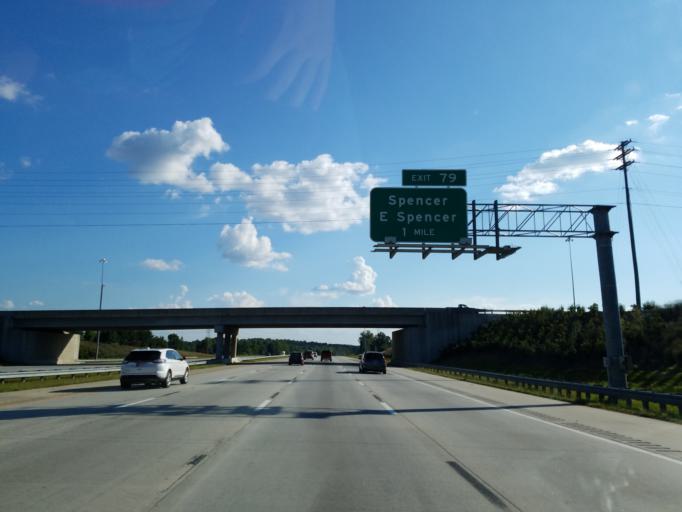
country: US
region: North Carolina
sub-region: Rowan County
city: Spencer
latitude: 35.6963
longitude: -80.4009
